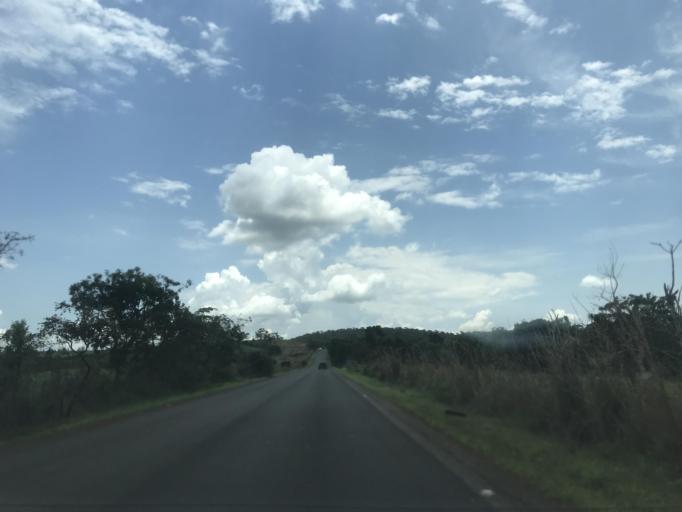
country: BR
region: Goias
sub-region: Vianopolis
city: Vianopolis
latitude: -16.9501
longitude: -48.5914
